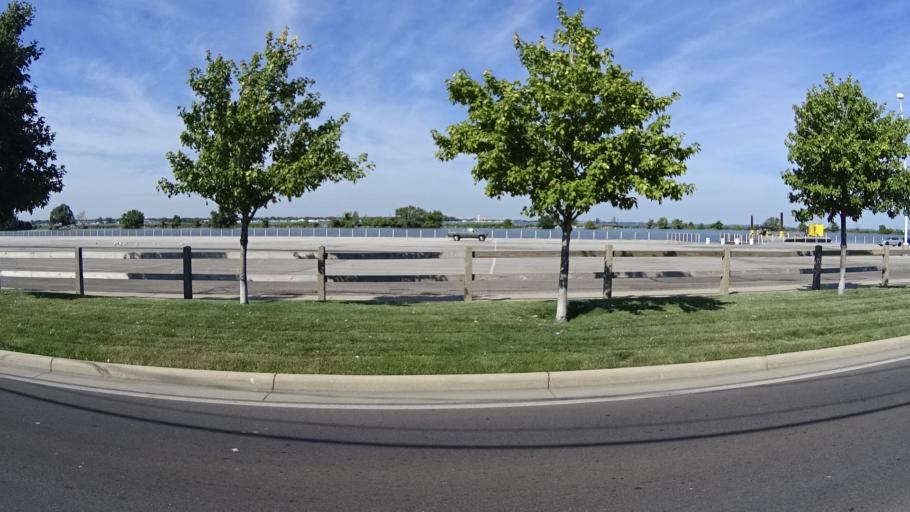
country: US
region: Ohio
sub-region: Erie County
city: Sandusky
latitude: 41.4734
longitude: -82.6781
